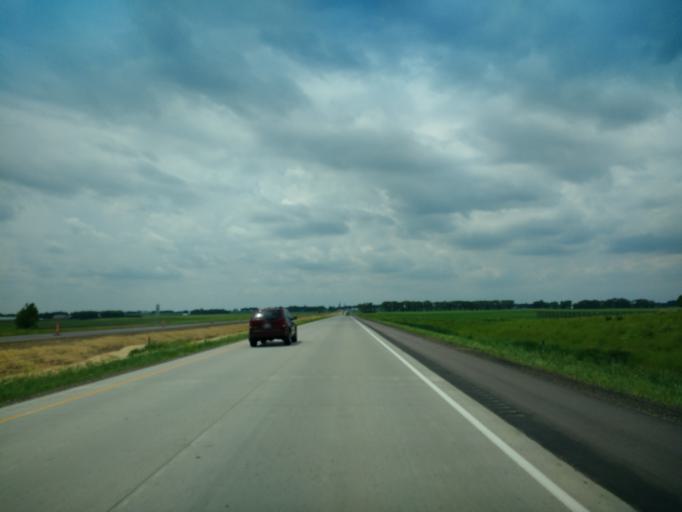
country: US
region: Minnesota
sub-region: Cottonwood County
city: Mountain Lake
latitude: 43.9177
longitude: -95.0037
